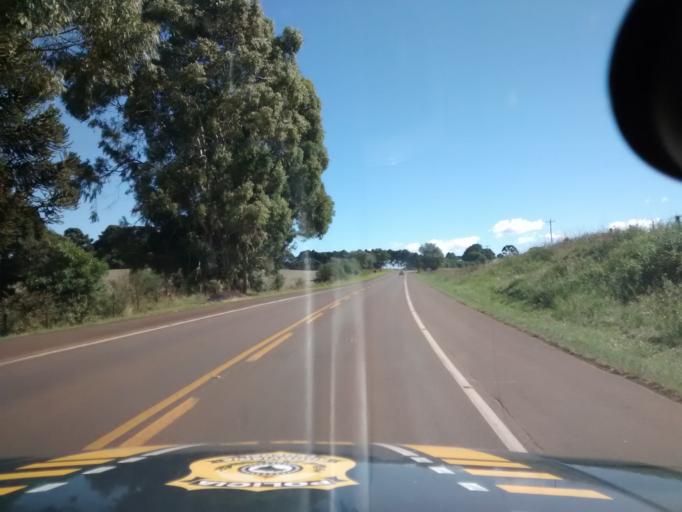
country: BR
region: Rio Grande do Sul
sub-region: Vacaria
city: Vacaria
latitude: -28.3553
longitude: -51.1179
